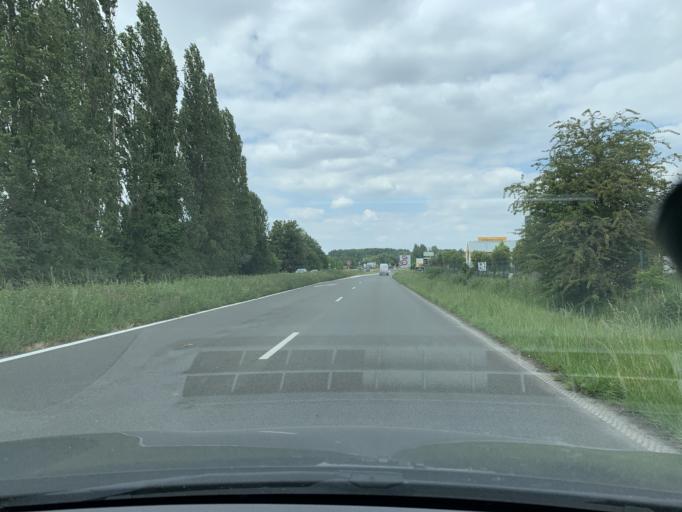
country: FR
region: Nord-Pas-de-Calais
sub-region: Departement du Nord
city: Cuincy
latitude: 50.3807
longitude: 3.0569
